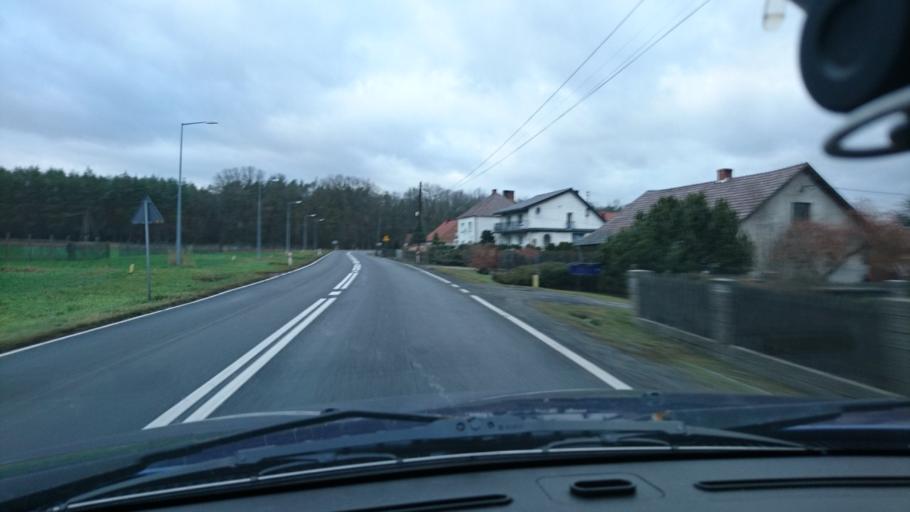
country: PL
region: Opole Voivodeship
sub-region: Powiat kluczborski
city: Kluczbork
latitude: 50.9468
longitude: 18.3176
